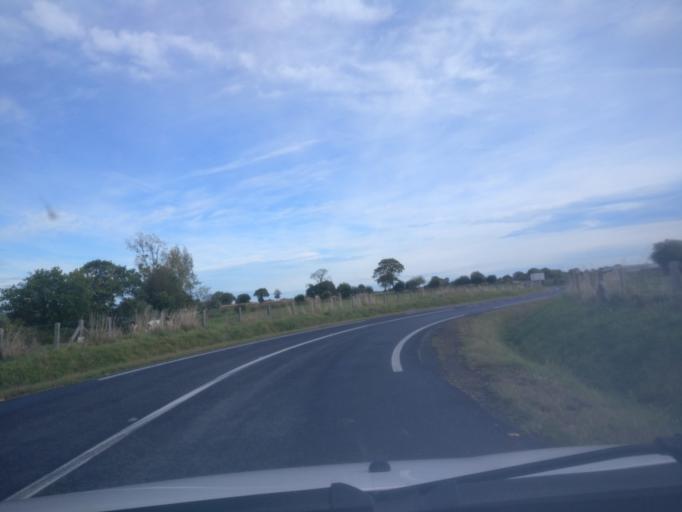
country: FR
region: Lower Normandy
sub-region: Departement de la Manche
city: Sartilly
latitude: 48.7511
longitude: -1.4720
